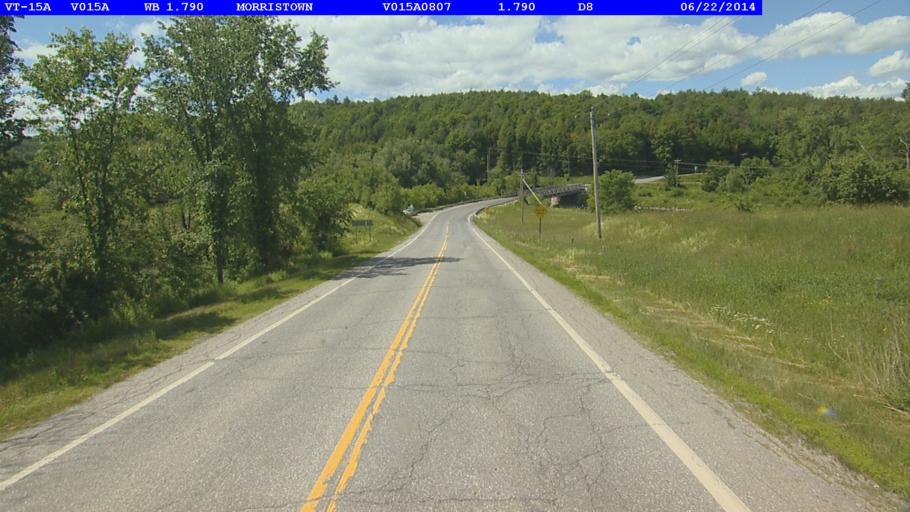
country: US
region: Vermont
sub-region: Lamoille County
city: Morrisville
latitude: 44.5654
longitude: -72.5644
